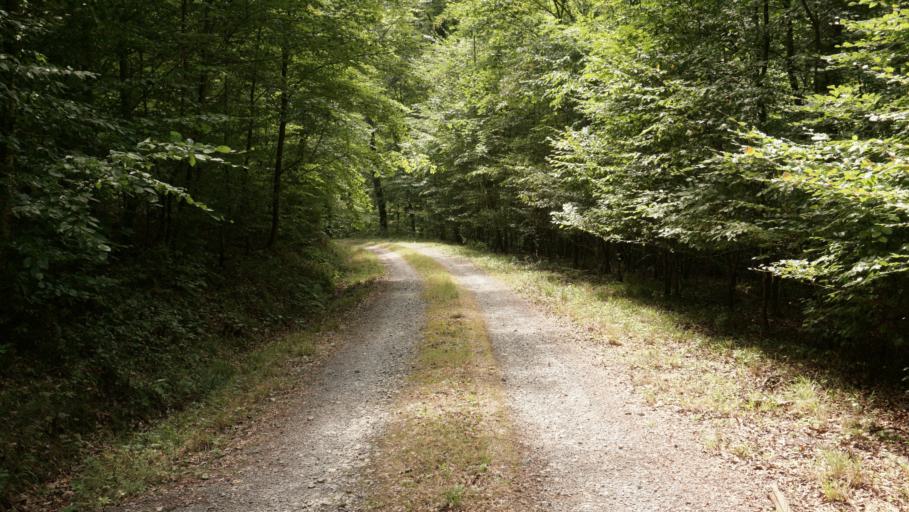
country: DE
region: Baden-Wuerttemberg
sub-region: Karlsruhe Region
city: Mosbach
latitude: 49.3868
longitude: 9.1535
